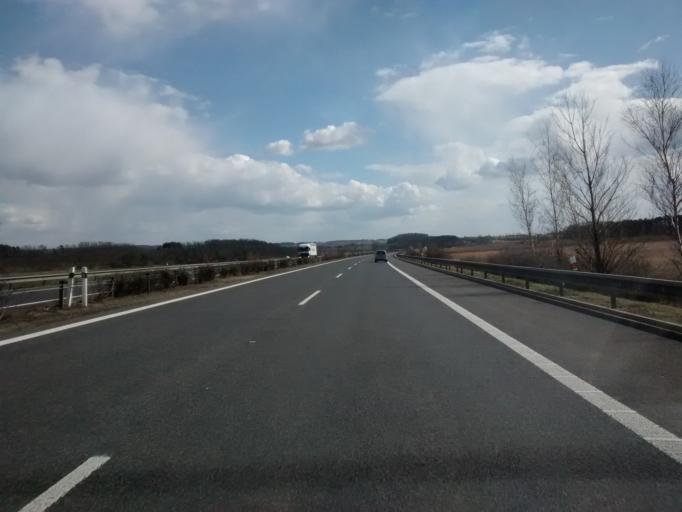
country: CZ
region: Ustecky
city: Roudnice nad Labem
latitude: 50.3856
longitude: 14.2394
